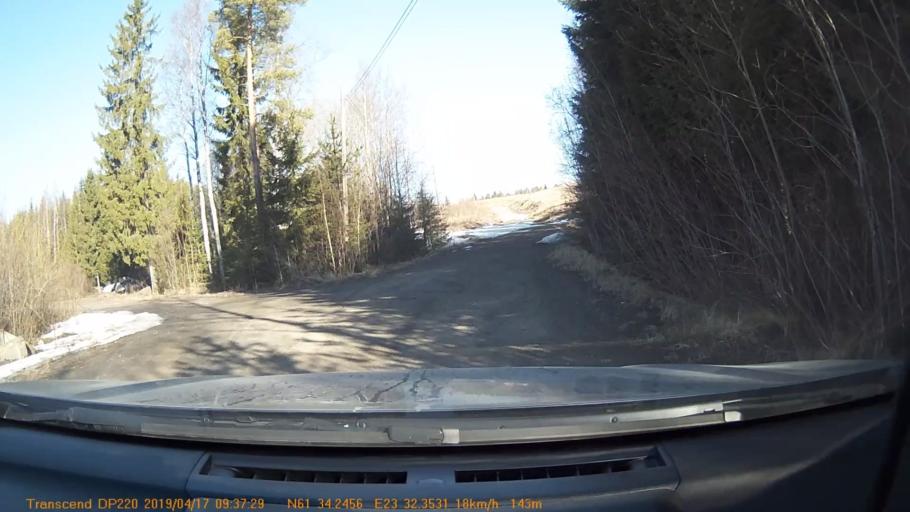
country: FI
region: Pirkanmaa
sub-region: Tampere
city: Yloejaervi
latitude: 61.5707
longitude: 23.5393
